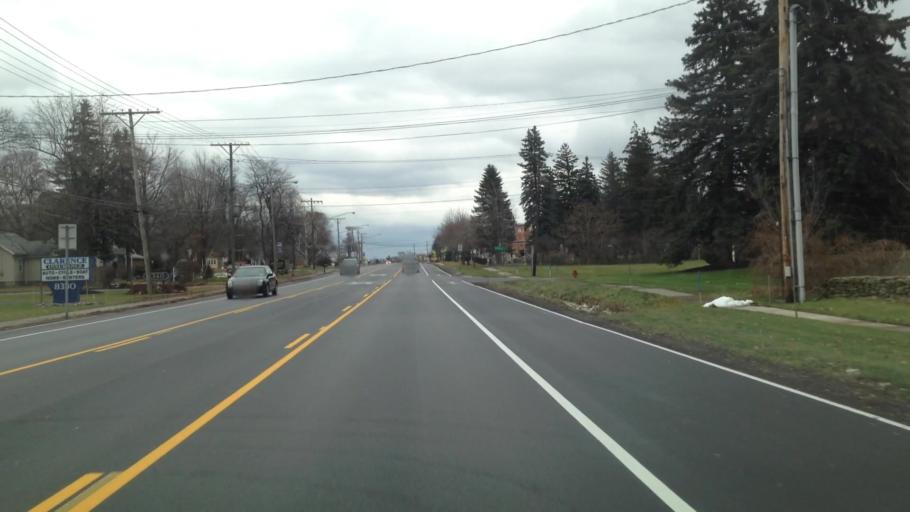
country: US
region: New York
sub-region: Erie County
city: Harris Hill
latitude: 42.9650
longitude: -78.6840
